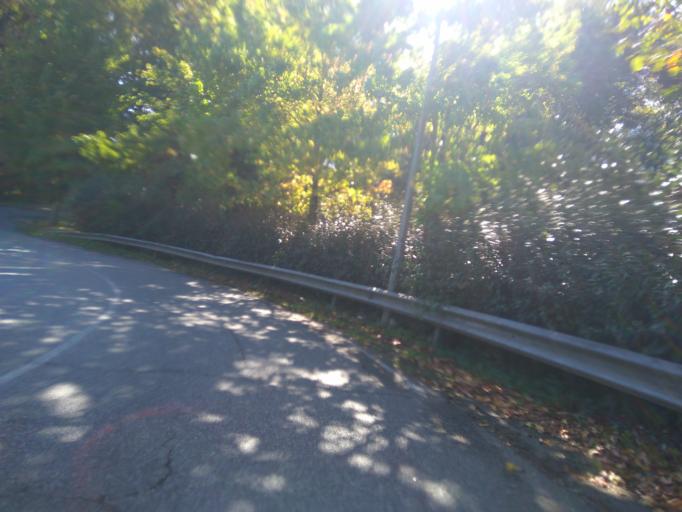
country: FR
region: Aquitaine
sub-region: Departement des Pyrenees-Atlantiques
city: Idron
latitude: 43.2961
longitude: -0.3120
